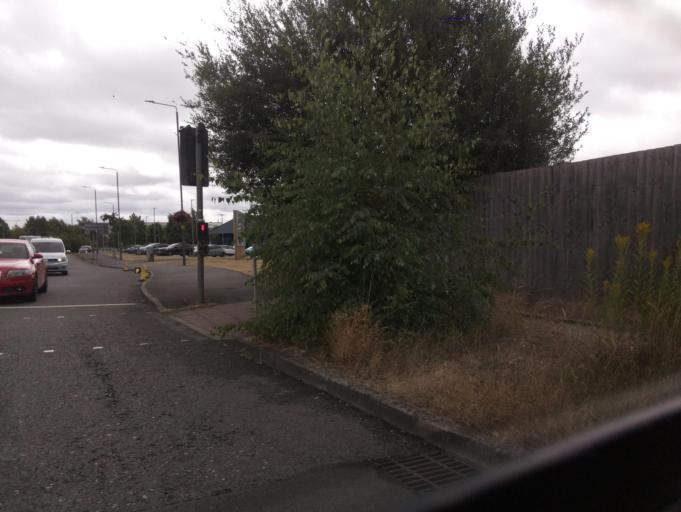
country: GB
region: England
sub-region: Derbyshire
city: Heanor
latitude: 53.0200
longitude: -1.3260
